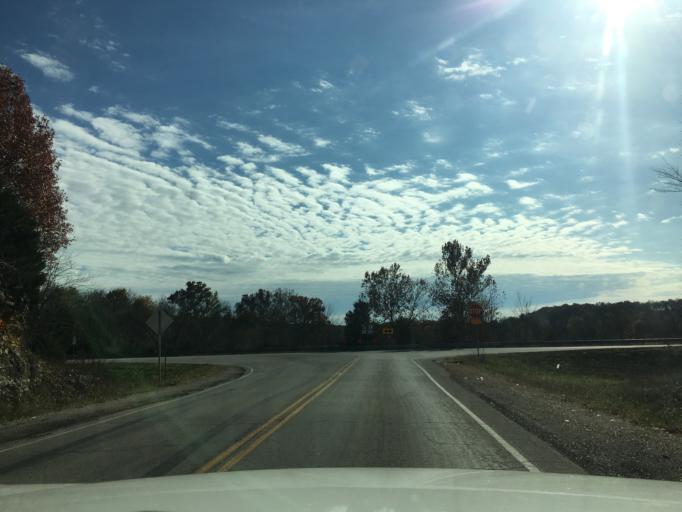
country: US
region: Missouri
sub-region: Osage County
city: Linn
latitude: 38.3902
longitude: -91.8243
